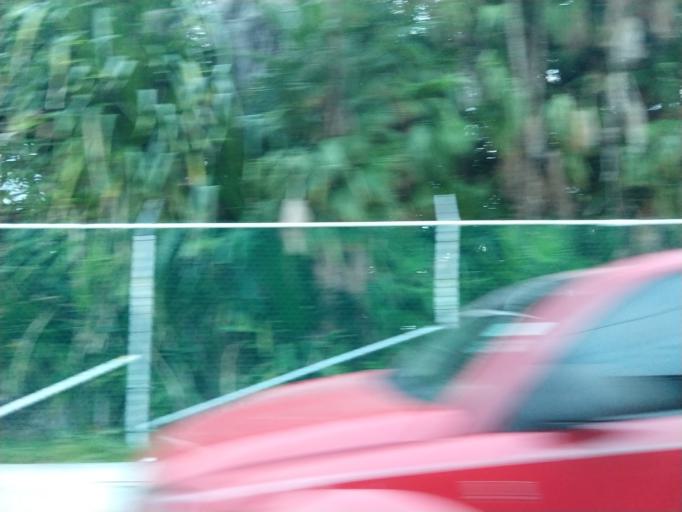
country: BZ
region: Belize
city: Belize City
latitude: 17.5061
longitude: -88.1884
